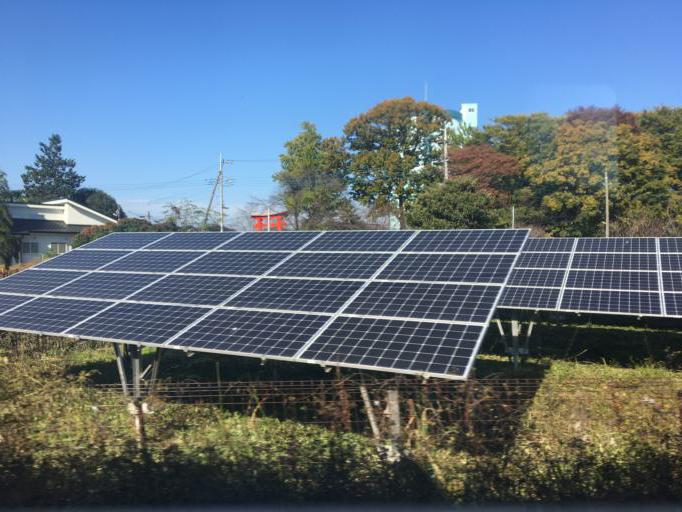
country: JP
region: Gunma
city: Isesaki
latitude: 36.3648
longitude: 139.2494
